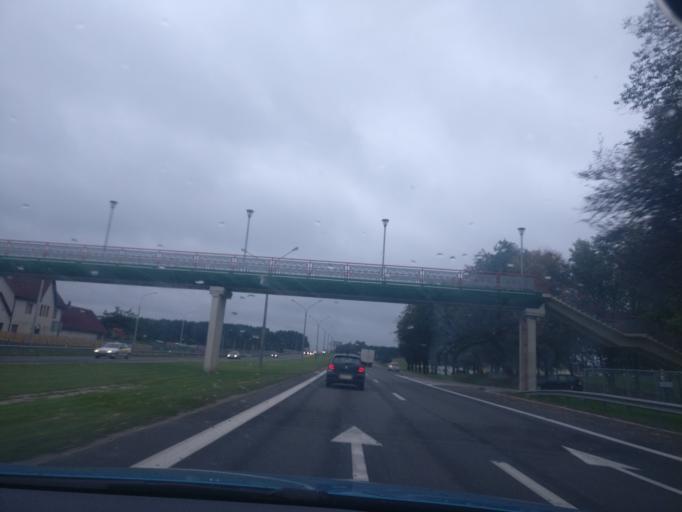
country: BY
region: Minsk
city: Korolev Stan
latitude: 53.9874
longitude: 27.7947
